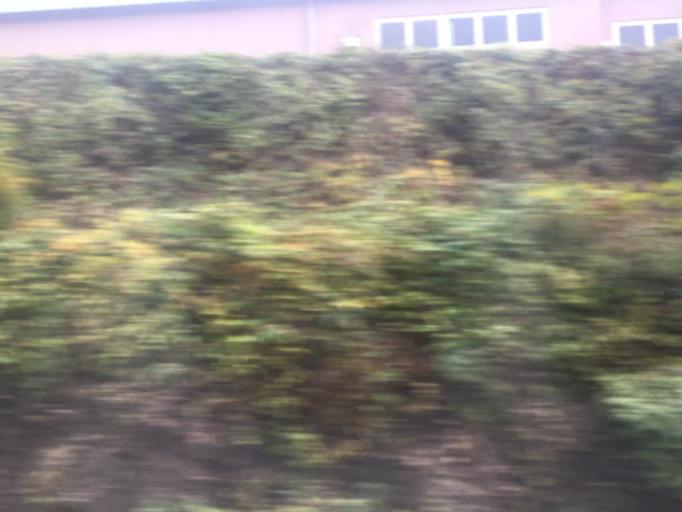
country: JP
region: Saitama
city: Hanno
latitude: 35.7976
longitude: 139.3353
